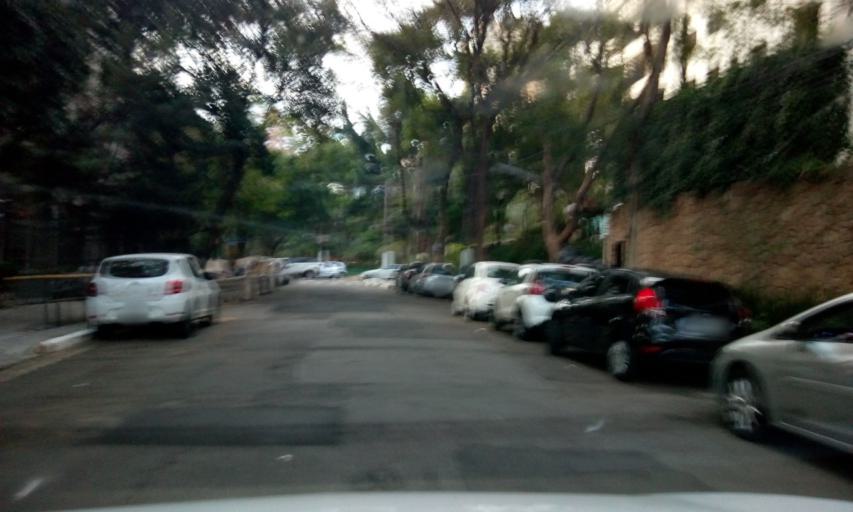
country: BR
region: Sao Paulo
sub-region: Sao Paulo
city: Sao Paulo
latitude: -23.5949
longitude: -46.6695
